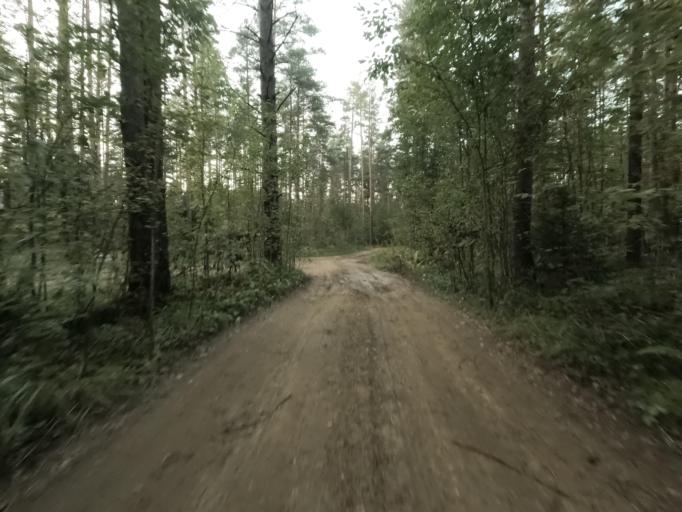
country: RU
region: Leningrad
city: Otradnoye
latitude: 59.8494
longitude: 30.7959
